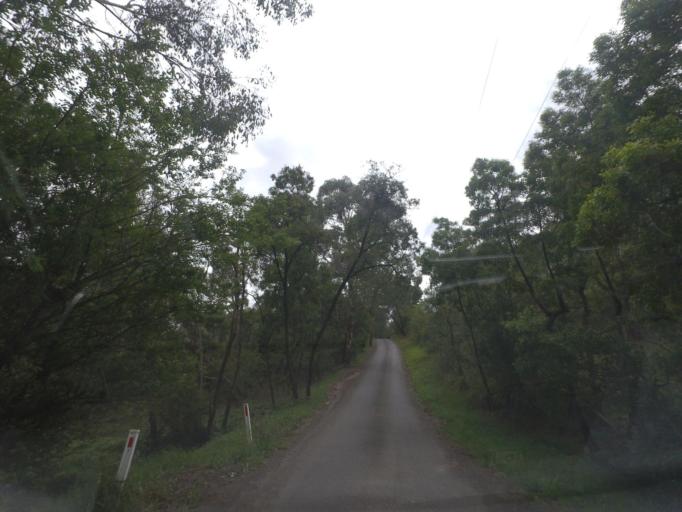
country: AU
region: Victoria
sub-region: Manningham
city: Park Orchards
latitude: -37.7766
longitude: 145.1973
